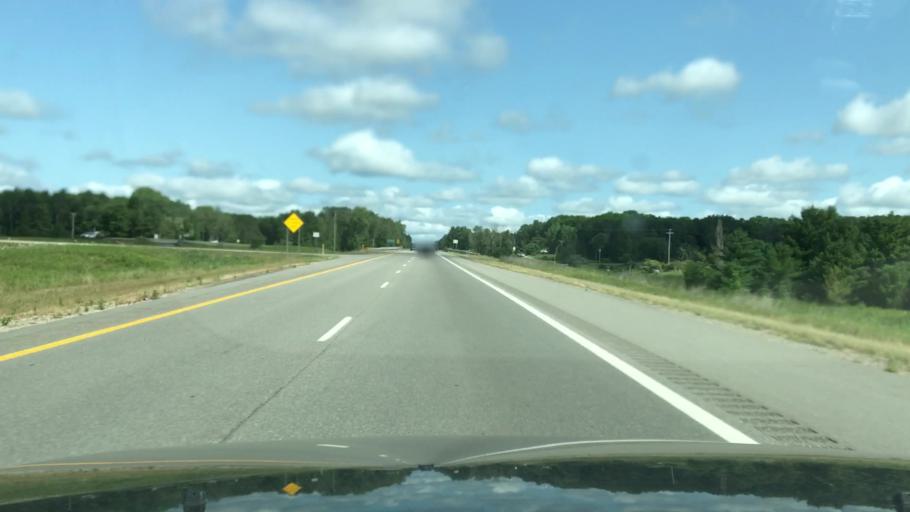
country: US
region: Michigan
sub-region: Mecosta County
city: Big Rapids
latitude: 43.6253
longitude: -85.5001
